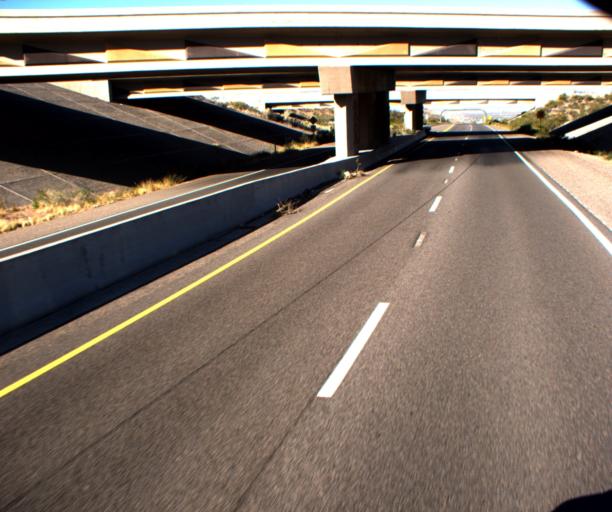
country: US
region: Arizona
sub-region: Mohave County
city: Kingman
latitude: 35.2219
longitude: -114.1254
